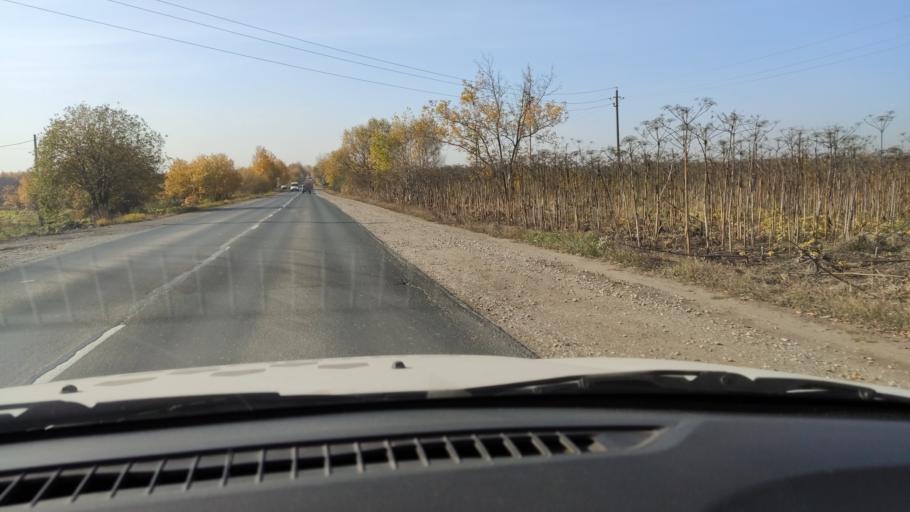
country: RU
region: Perm
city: Perm
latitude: 58.0373
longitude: 56.3810
